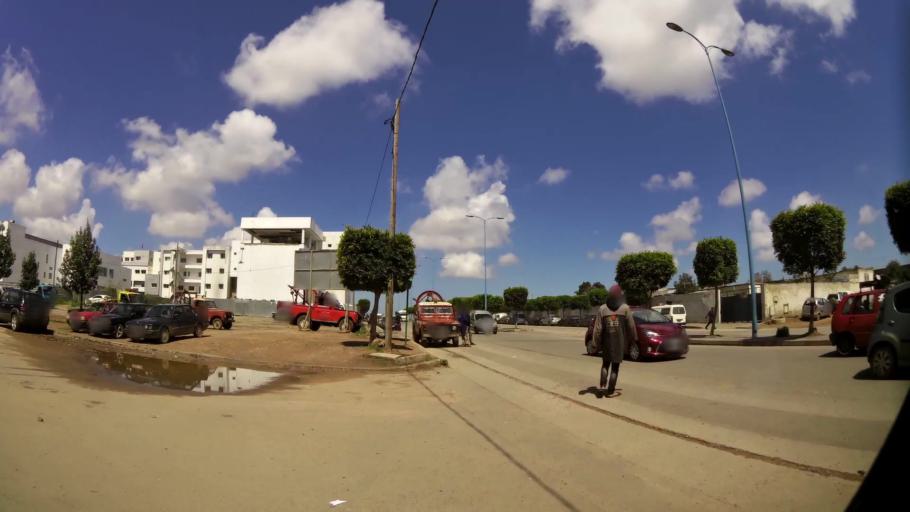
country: MA
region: Grand Casablanca
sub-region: Casablanca
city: Casablanca
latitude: 33.5395
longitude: -7.5574
